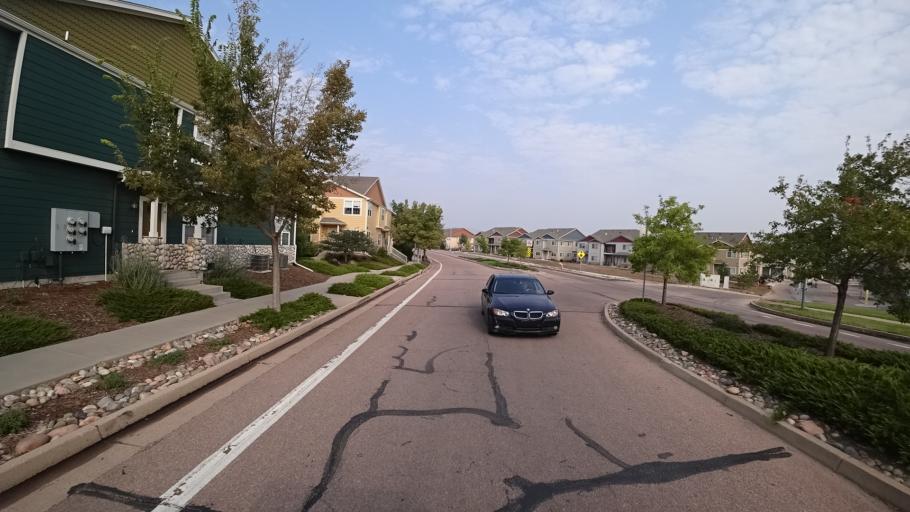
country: US
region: Colorado
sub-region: El Paso County
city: Stratmoor
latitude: 38.8072
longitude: -104.7831
